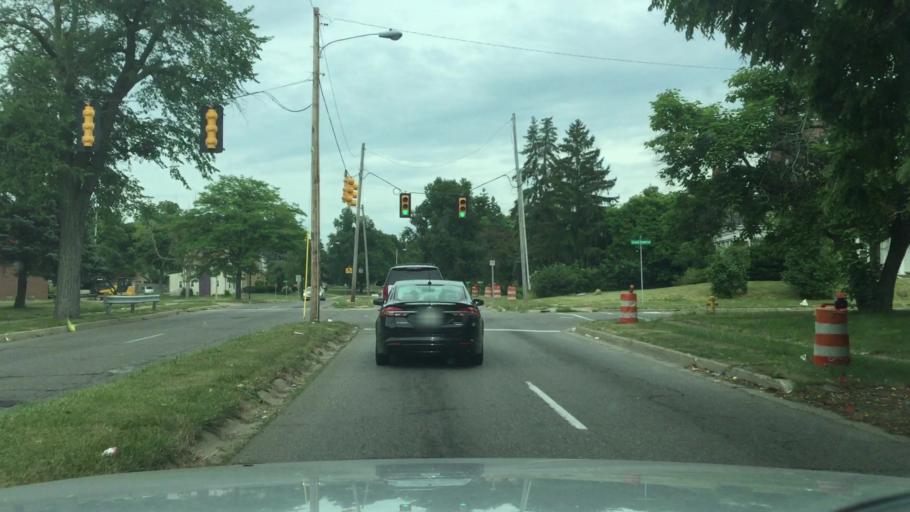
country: US
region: Michigan
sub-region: Genesee County
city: Flint
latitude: 43.0308
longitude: -83.7092
